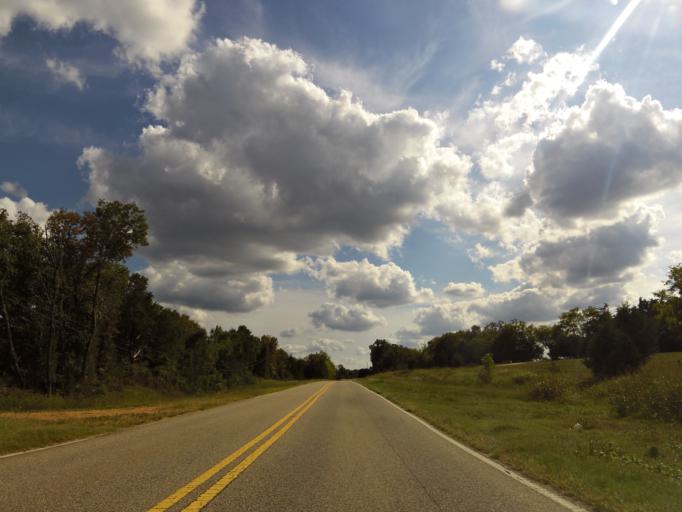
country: US
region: Alabama
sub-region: Dallas County
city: Selmont-West Selmont
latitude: 32.2297
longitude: -86.9952
